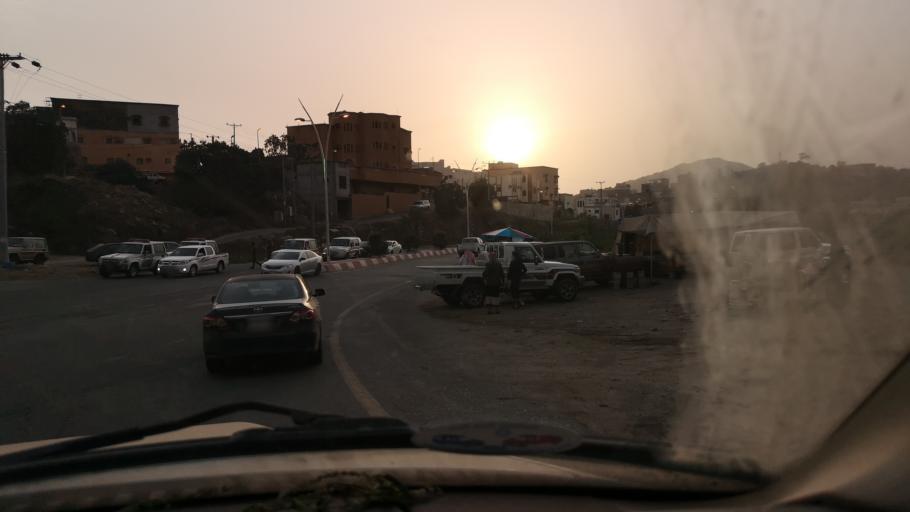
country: YE
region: Sa'dah
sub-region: Monabbih
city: Suq al Khamis
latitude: 17.3449
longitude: 43.1496
